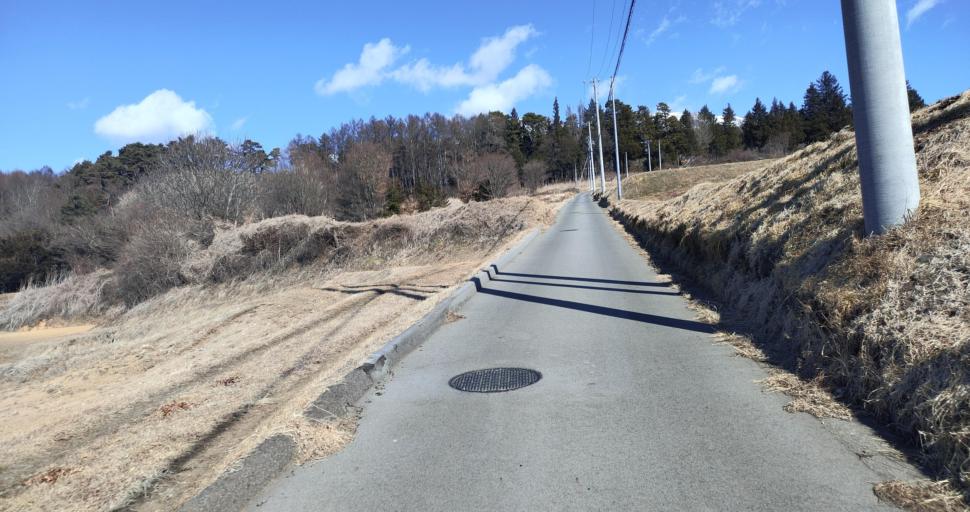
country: JP
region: Nagano
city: Komoro
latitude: 36.3408
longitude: 138.4941
